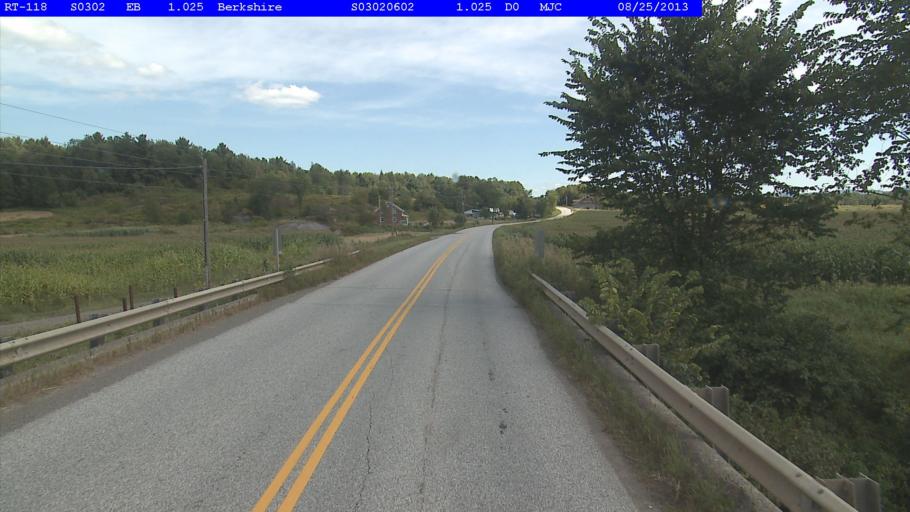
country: US
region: Vermont
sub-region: Franklin County
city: Enosburg Falls
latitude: 44.9834
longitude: -72.7952
